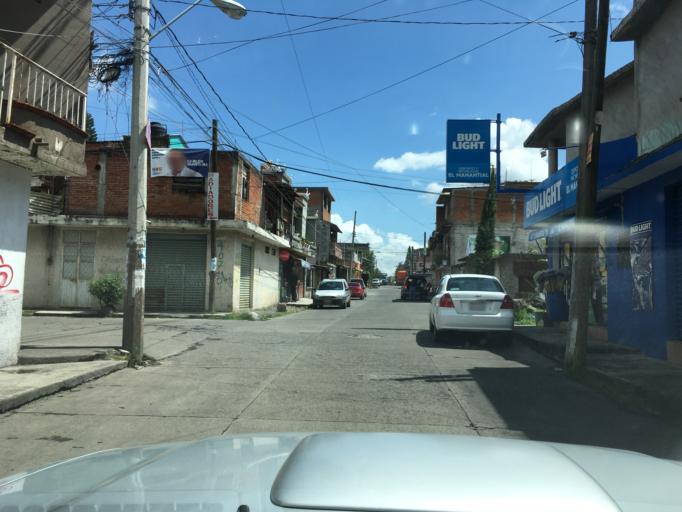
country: MX
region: Michoacan
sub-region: Tarimbaro
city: Real Hacienda (Metropolis)
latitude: 19.7296
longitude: -101.2042
